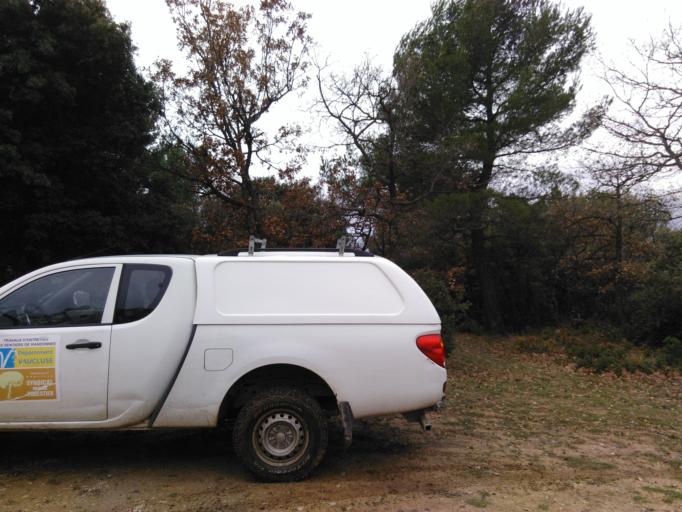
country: FR
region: Provence-Alpes-Cote d'Azur
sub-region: Departement du Vaucluse
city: Sablet
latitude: 44.1975
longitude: 5.0500
